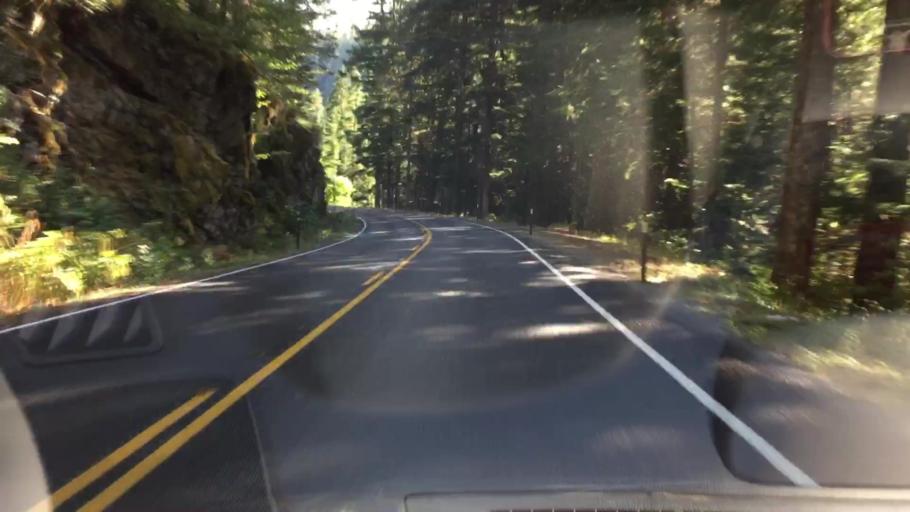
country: US
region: Washington
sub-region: Pierce County
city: Buckley
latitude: 46.7020
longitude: -121.5816
